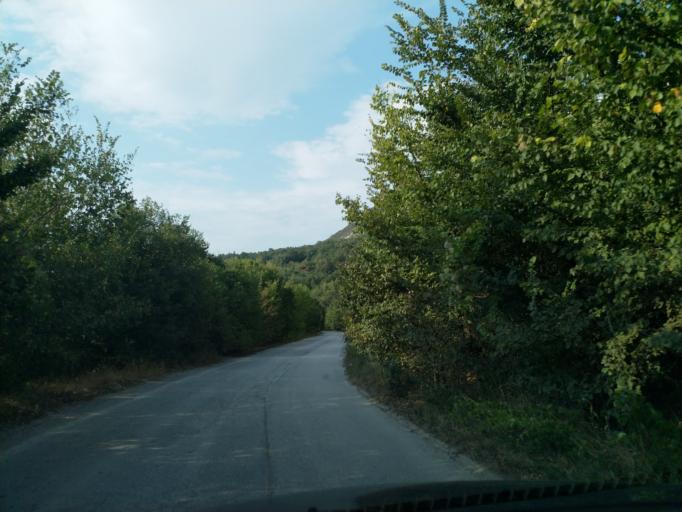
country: RS
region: Central Serbia
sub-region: Pomoravski Okrug
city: Paracin
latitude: 43.8387
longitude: 21.5388
